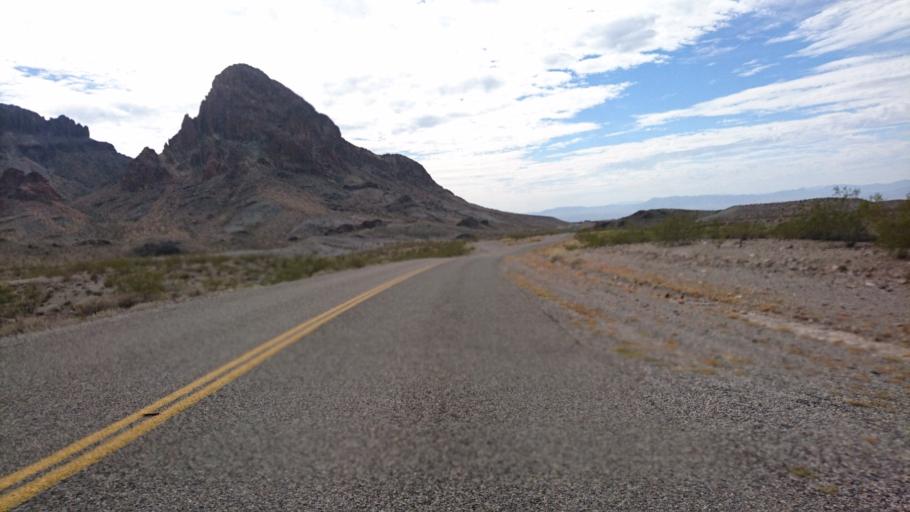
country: US
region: Arizona
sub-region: Mohave County
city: Mohave Valley
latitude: 34.9971
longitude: -114.4115
